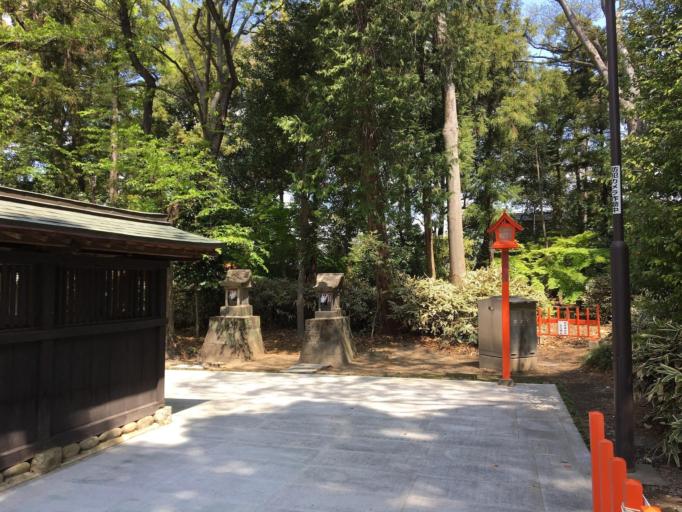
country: JP
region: Gunma
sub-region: Sawa-gun
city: Tamamura
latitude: 36.3051
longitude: 139.1090
